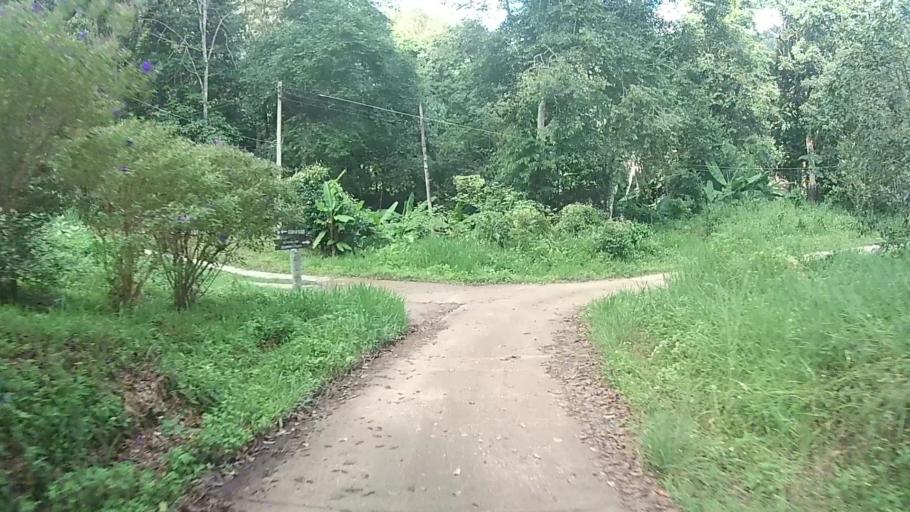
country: TH
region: Lampang
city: Mueang Pan
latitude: 18.9301
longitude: 99.4093
